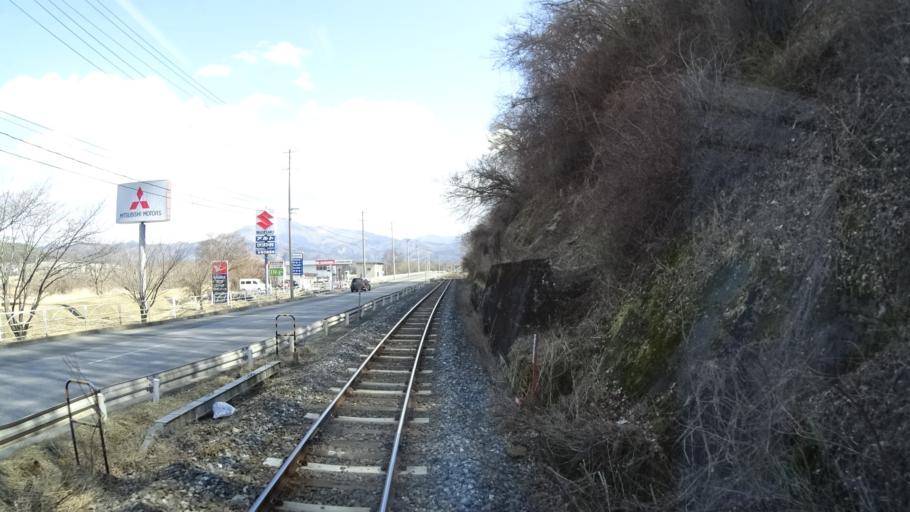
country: JP
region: Iwate
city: Tono
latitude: 39.3319
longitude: 141.5443
